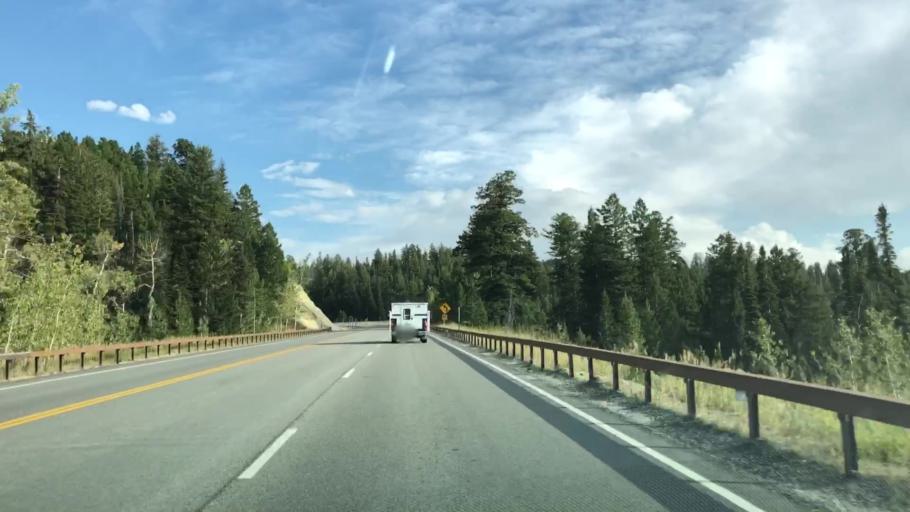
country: US
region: Wyoming
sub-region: Sublette County
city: Pinedale
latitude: 43.1352
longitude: -110.2070
